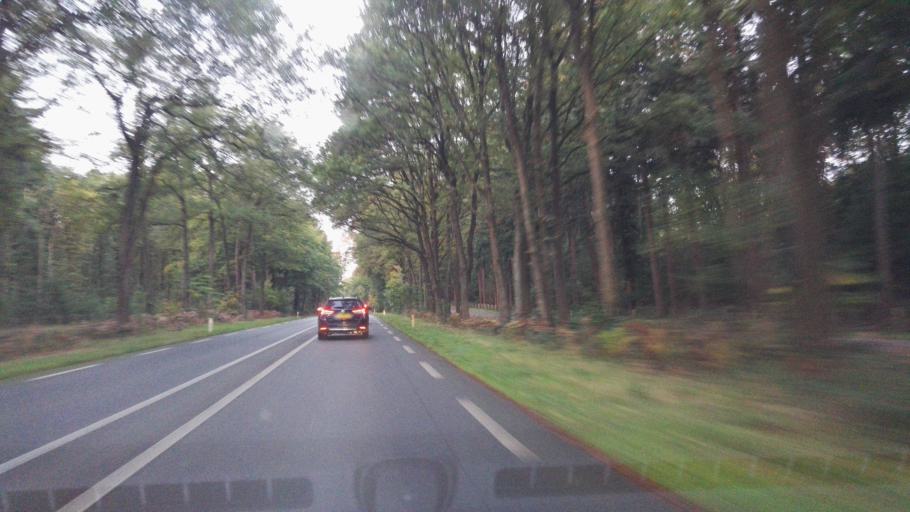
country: NL
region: Gelderland
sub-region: Gemeente Ede
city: Wekerom
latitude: 52.0810
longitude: 5.7162
